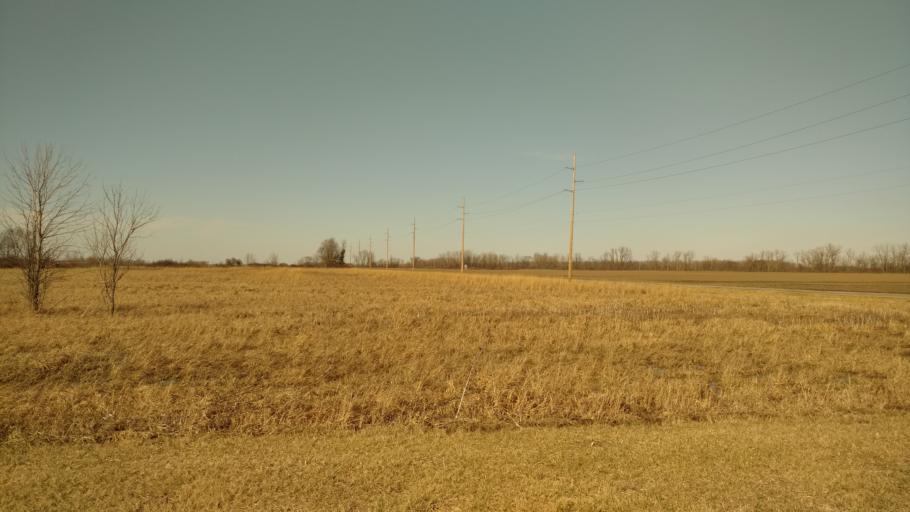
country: US
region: Ohio
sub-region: Wyandot County
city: Upper Sandusky
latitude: 40.6943
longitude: -83.2993
